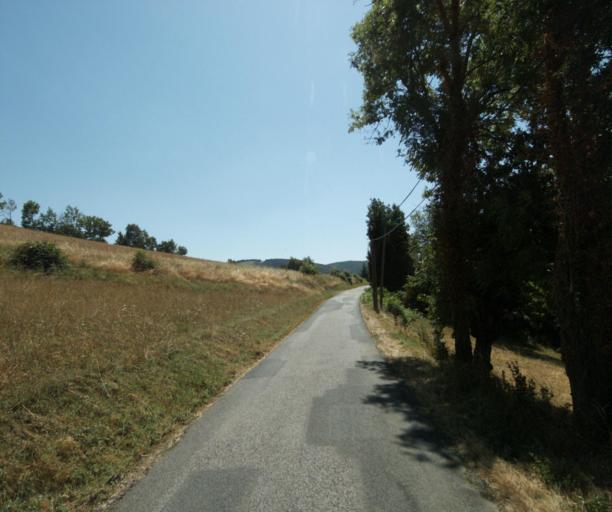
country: FR
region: Rhone-Alpes
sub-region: Departement du Rhone
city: Courzieu
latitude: 45.7524
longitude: 4.5814
